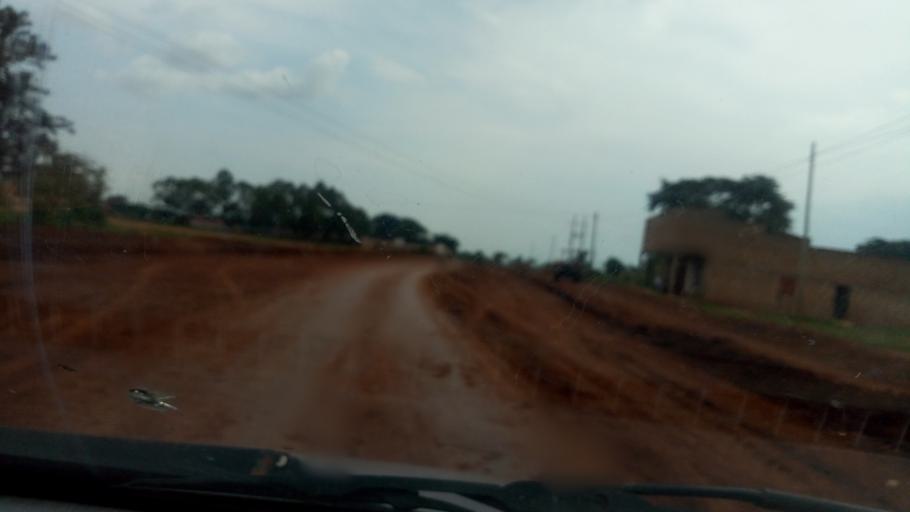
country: UG
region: Western Region
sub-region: Kiryandongo District
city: Kiryandongo
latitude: 1.8085
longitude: 32.0063
